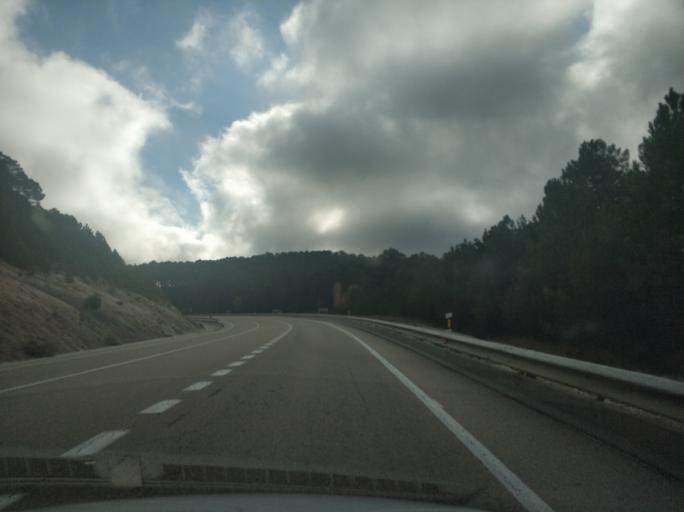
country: ES
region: Castille and Leon
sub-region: Provincia de Soria
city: Navaleno
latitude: 41.8290
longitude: -2.9675
